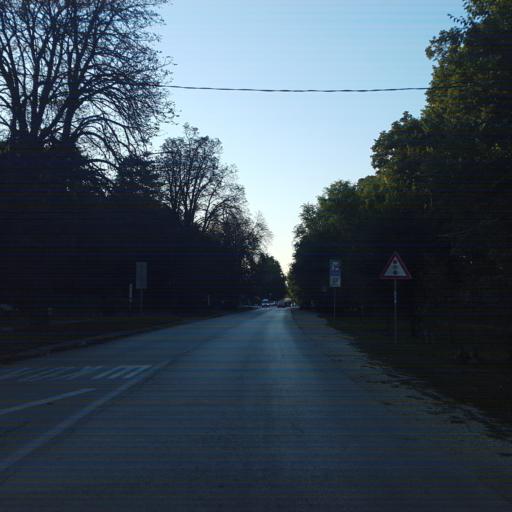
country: RS
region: Central Serbia
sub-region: Borski Okrug
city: Negotin
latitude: 44.2327
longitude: 22.5266
